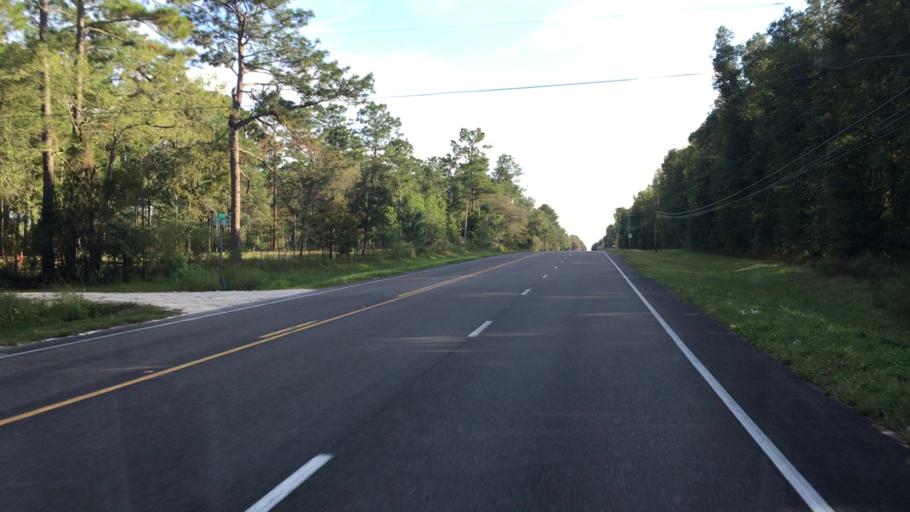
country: US
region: Florida
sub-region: Alachua County
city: Gainesville
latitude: 29.7286
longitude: -82.2769
